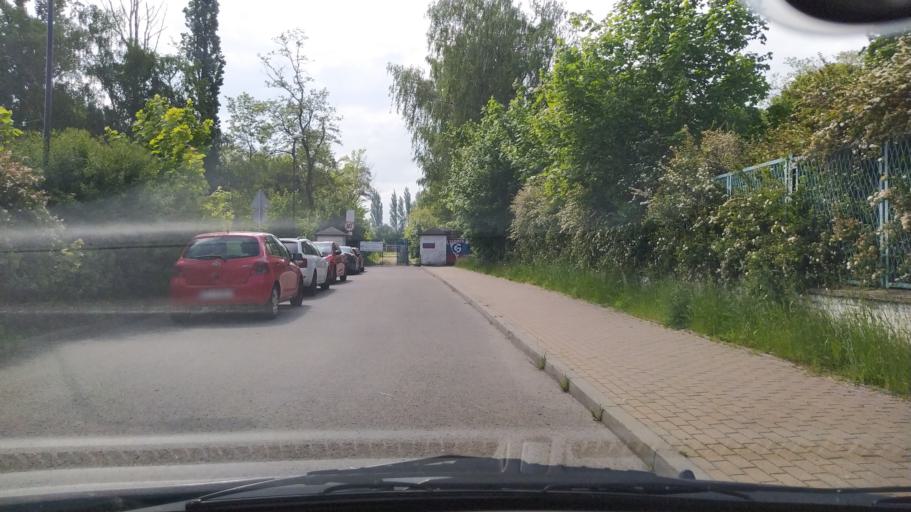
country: PL
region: Silesian Voivodeship
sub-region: Powiat gliwicki
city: Przyszowice
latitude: 50.2861
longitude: 18.7358
